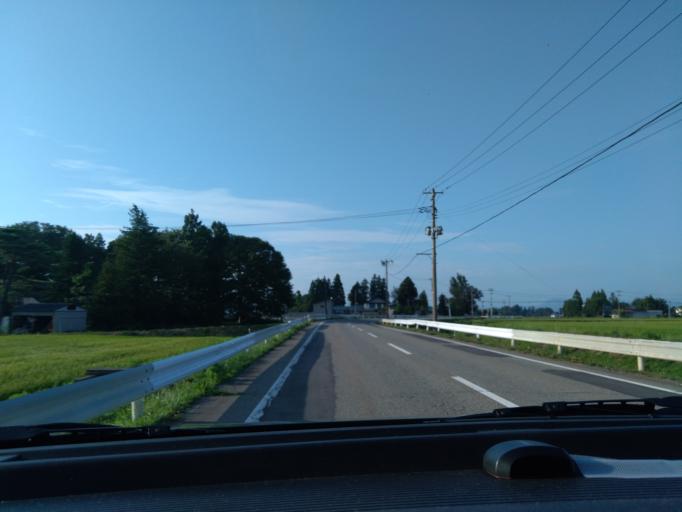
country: JP
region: Akita
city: Kakunodatemachi
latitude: 39.5259
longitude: 140.5578
